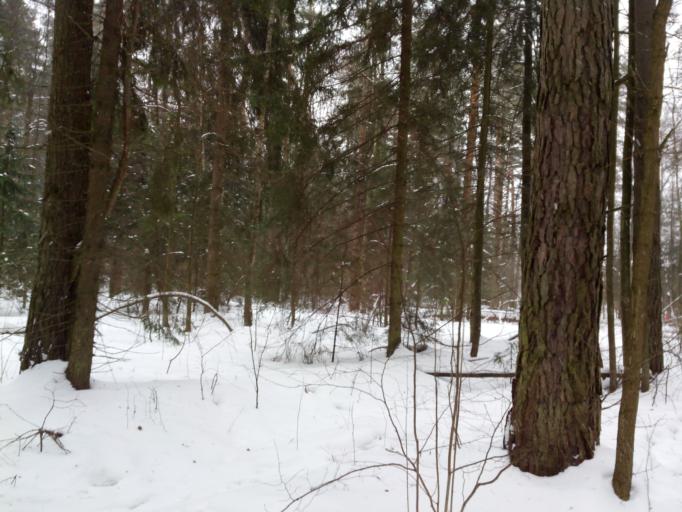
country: RU
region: Moskovskaya
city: Bol'shiye Vyazemy
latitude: 55.6641
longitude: 36.9886
